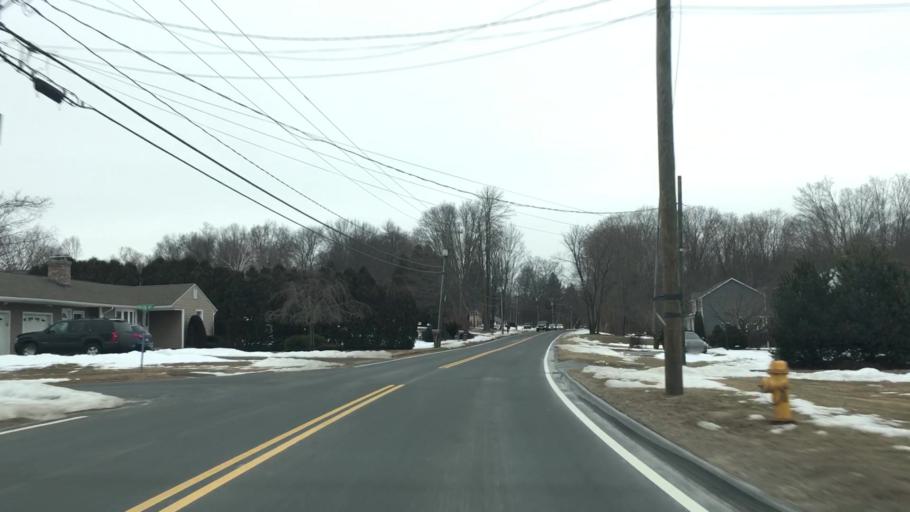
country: US
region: Massachusetts
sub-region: Hampden County
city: West Springfield
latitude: 42.0907
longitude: -72.6833
